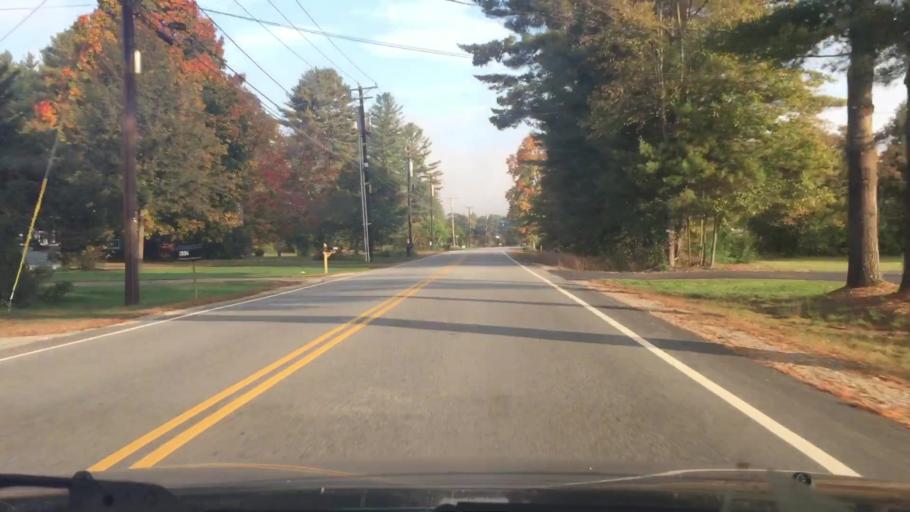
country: US
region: New Hampshire
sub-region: Cheshire County
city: Swanzey
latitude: 42.8567
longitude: -72.2790
